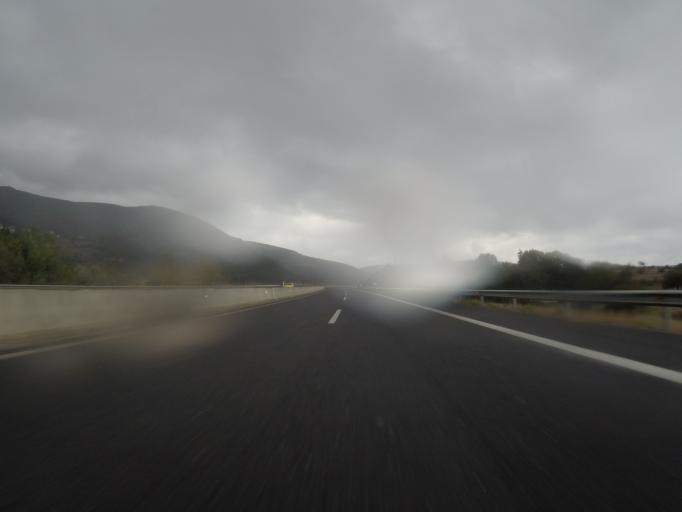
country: GR
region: Peloponnese
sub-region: Nomos Arkadias
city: Megalopoli
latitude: 37.3868
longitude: 22.2270
